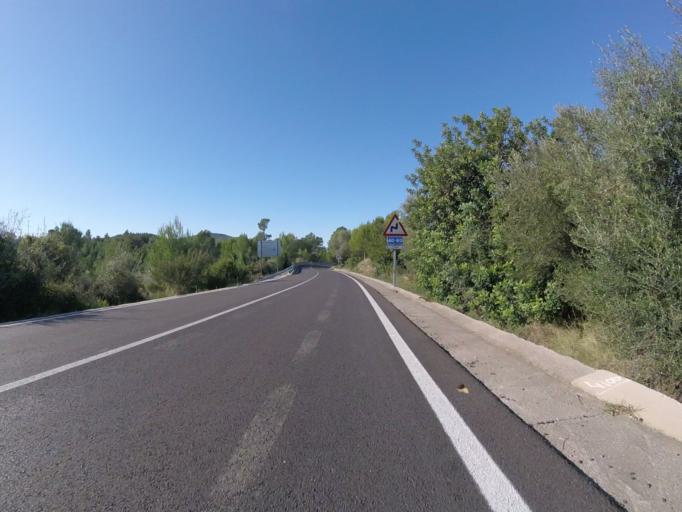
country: ES
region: Valencia
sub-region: Provincia de Castello
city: Cervera del Maestre
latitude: 40.4768
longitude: 0.2154
